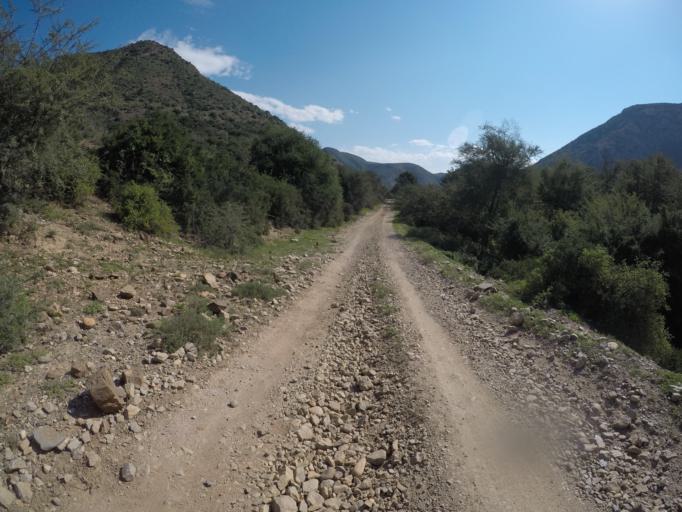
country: ZA
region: Eastern Cape
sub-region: Cacadu District Municipality
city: Kareedouw
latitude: -33.6668
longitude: 24.3797
